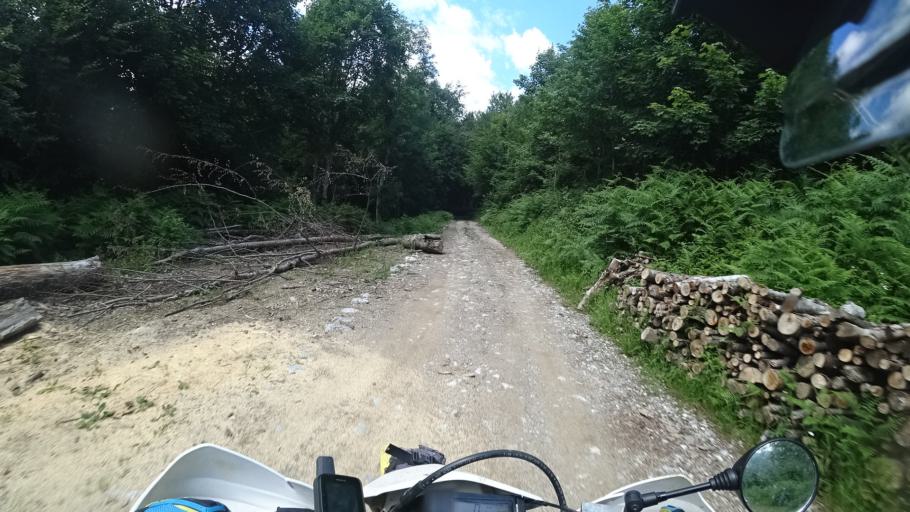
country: SI
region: Osilnica
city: Osilnica
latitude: 45.5106
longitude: 14.6631
